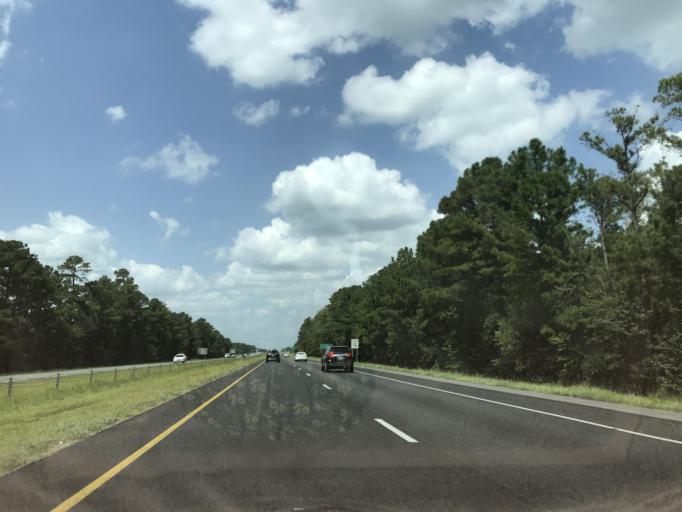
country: US
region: North Carolina
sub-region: Duplin County
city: Wallace
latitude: 34.7627
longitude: -77.9581
